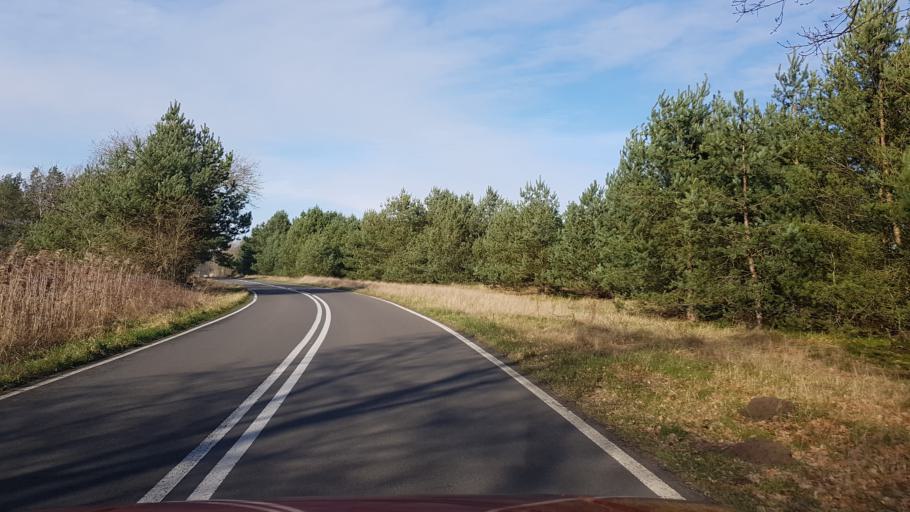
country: PL
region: West Pomeranian Voivodeship
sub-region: Powiat policki
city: Nowe Warpno
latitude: 53.7276
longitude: 14.3123
